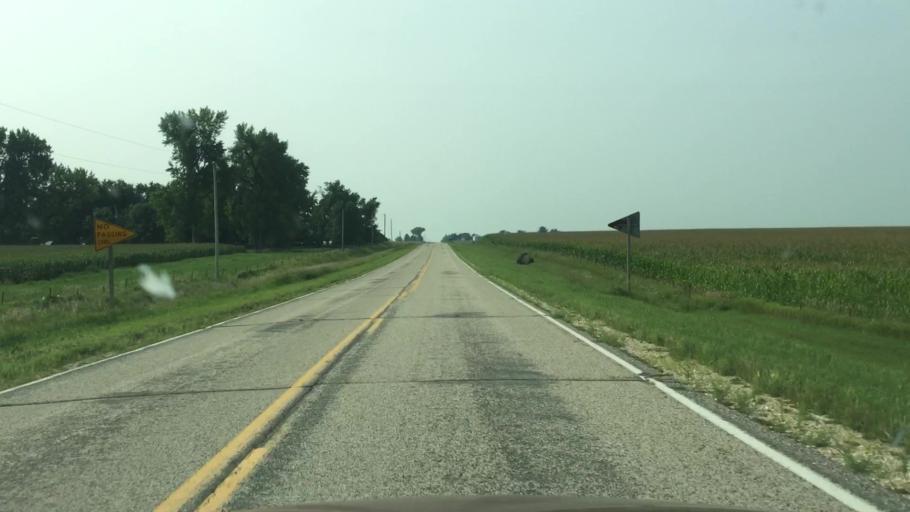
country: US
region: Iowa
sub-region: O'Brien County
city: Sheldon
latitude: 43.2794
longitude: -95.7829
